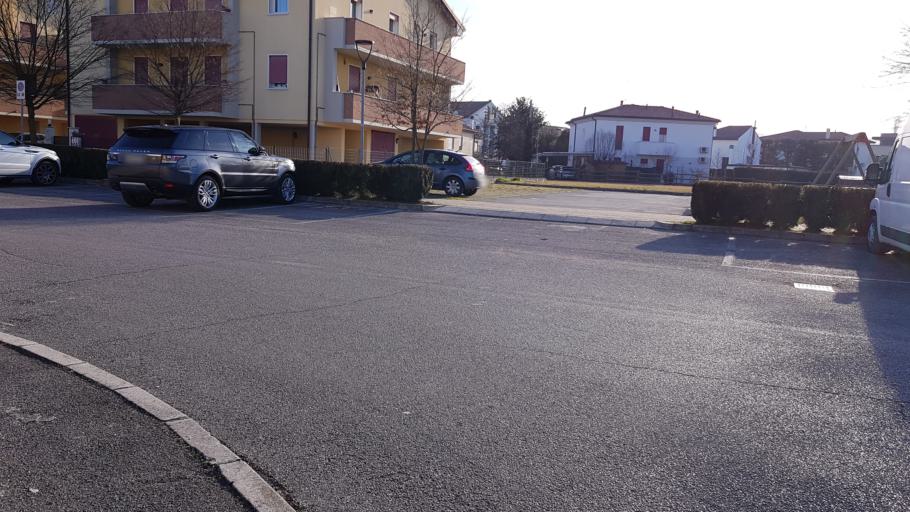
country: IT
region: Veneto
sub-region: Provincia di Padova
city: San Giorgio delle Pertiche
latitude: 45.5417
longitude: 11.9077
